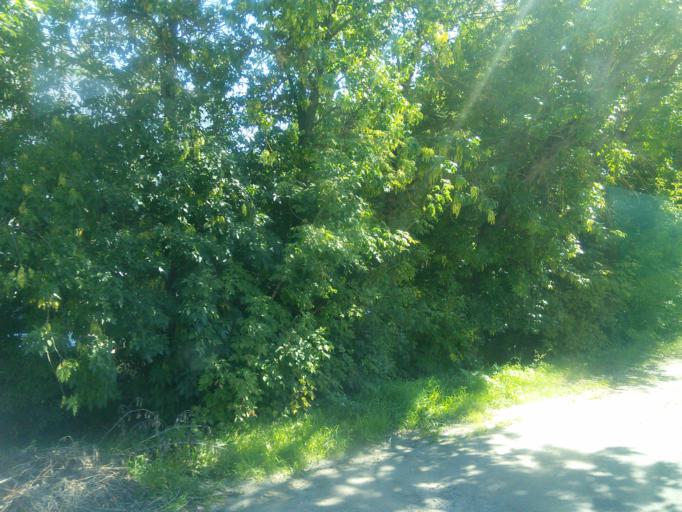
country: RU
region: Tverskaya
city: Kashin
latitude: 57.3631
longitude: 37.6134
